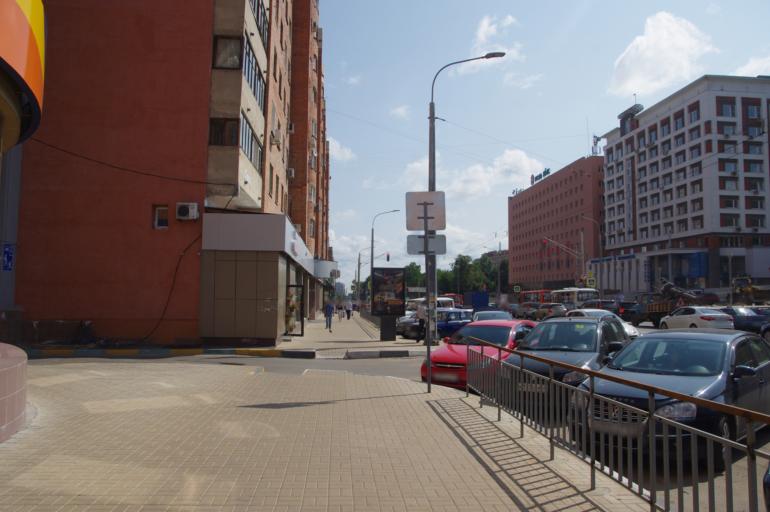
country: RU
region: Nizjnij Novgorod
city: Nizhniy Novgorod
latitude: 56.3151
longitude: 43.9986
